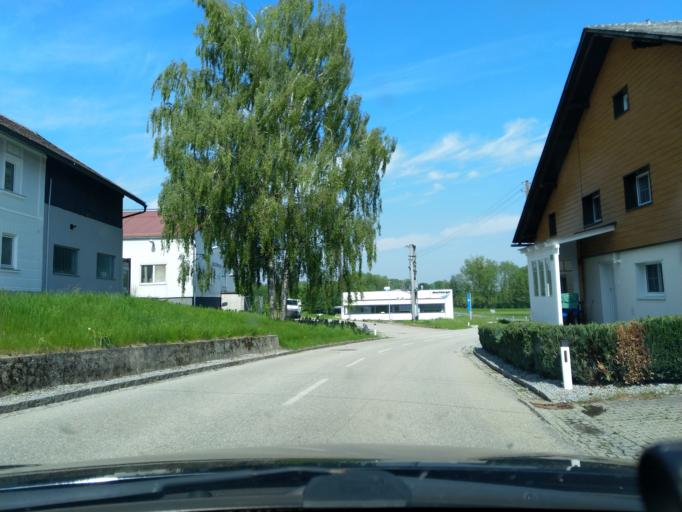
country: AT
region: Upper Austria
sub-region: Politischer Bezirk Scharding
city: Sankt Marienkirchen bei Schaerding
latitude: 48.3016
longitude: 13.4122
